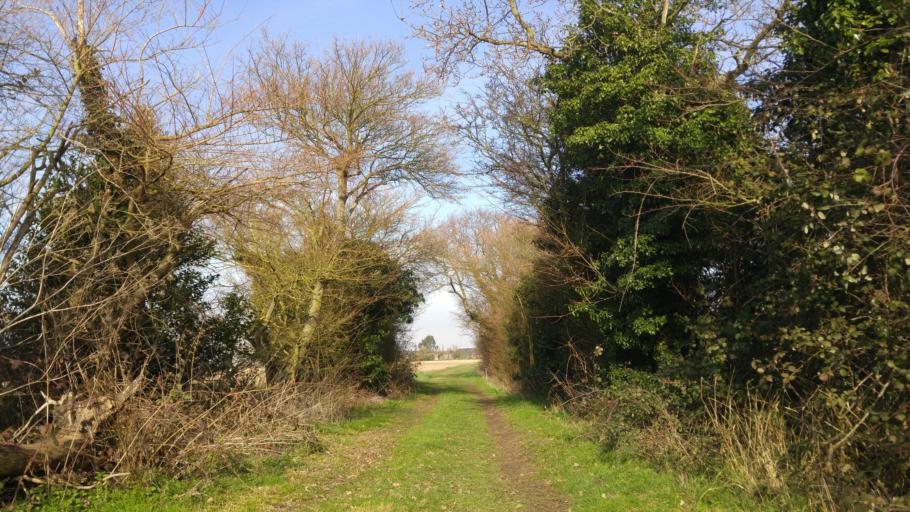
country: GB
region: England
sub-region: Essex
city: Little Clacton
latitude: 51.8220
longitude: 1.1706
